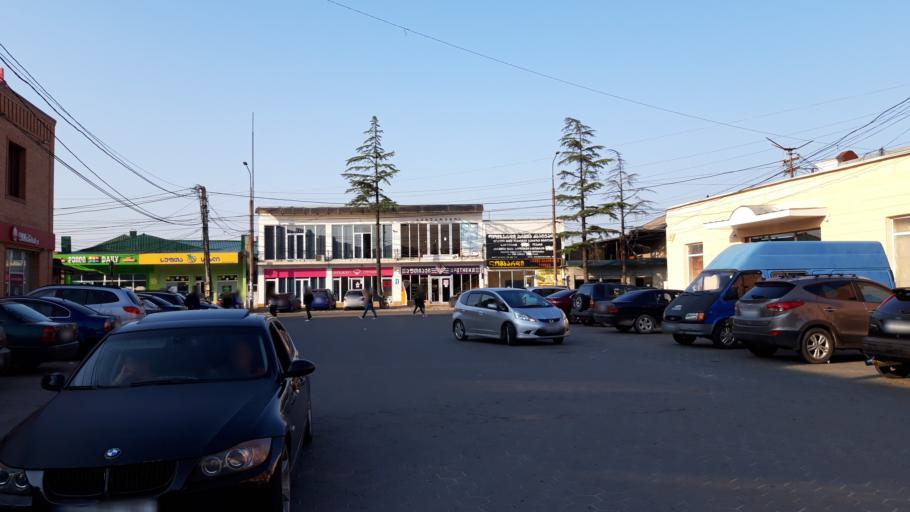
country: GE
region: Imereti
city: Samtredia
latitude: 42.1639
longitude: 42.3425
